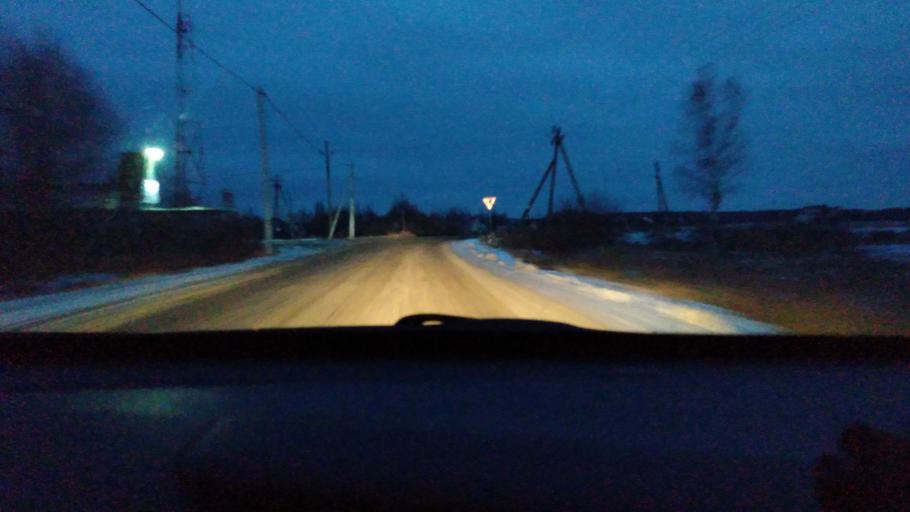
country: RU
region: Moskovskaya
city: Meshcherino
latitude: 55.2918
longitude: 38.3436
